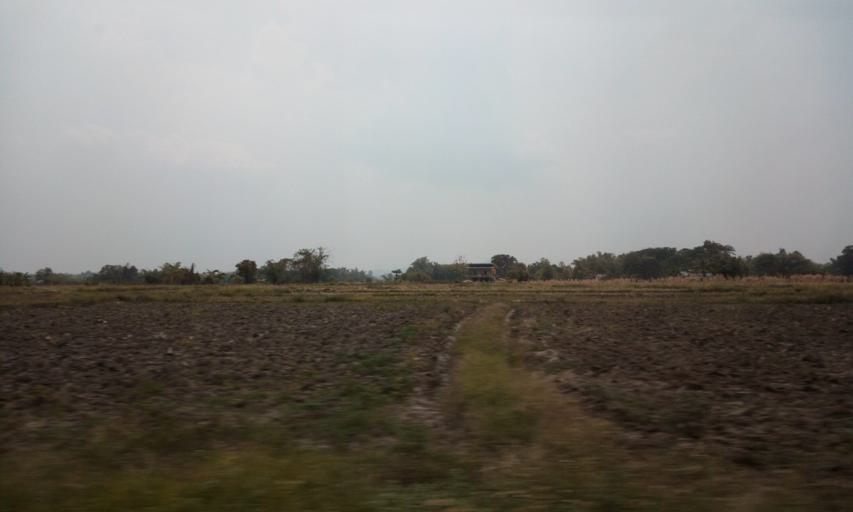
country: TH
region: Phayao
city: Phu Sang
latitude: 19.6063
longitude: 100.3219
